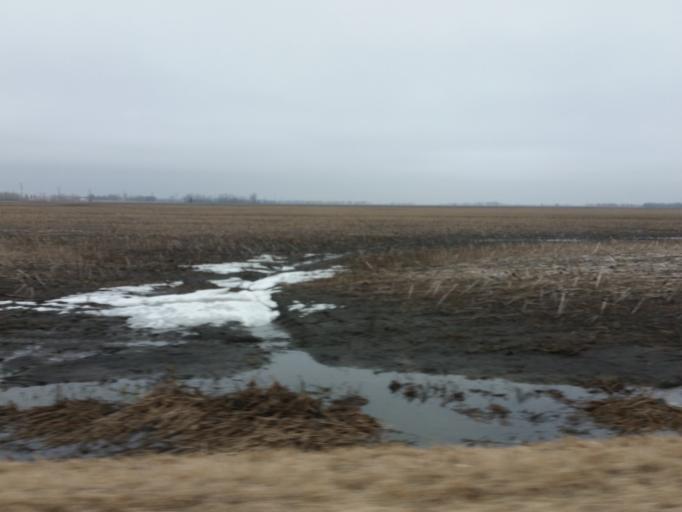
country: US
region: North Dakota
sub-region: Walsh County
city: Grafton
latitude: 48.3566
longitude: -97.1674
